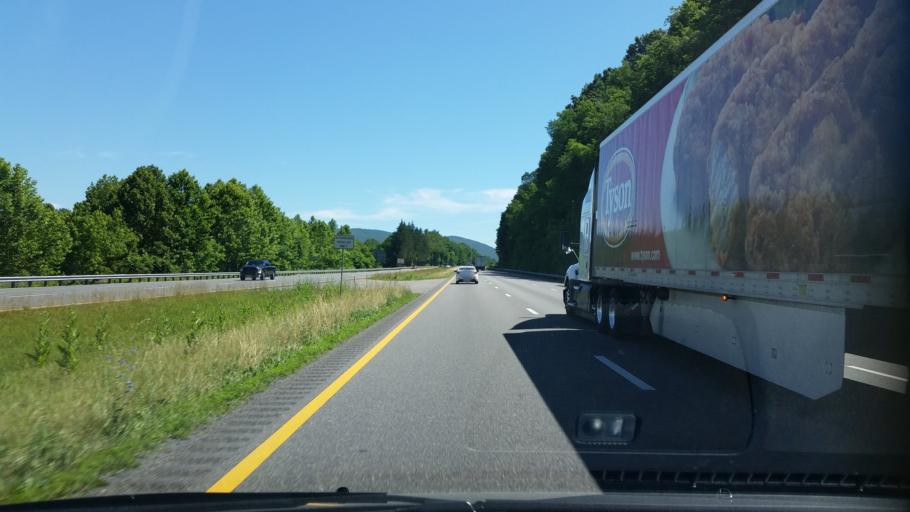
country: US
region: Virginia
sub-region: Smyth County
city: Chilhowie
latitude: 36.7964
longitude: -81.6785
